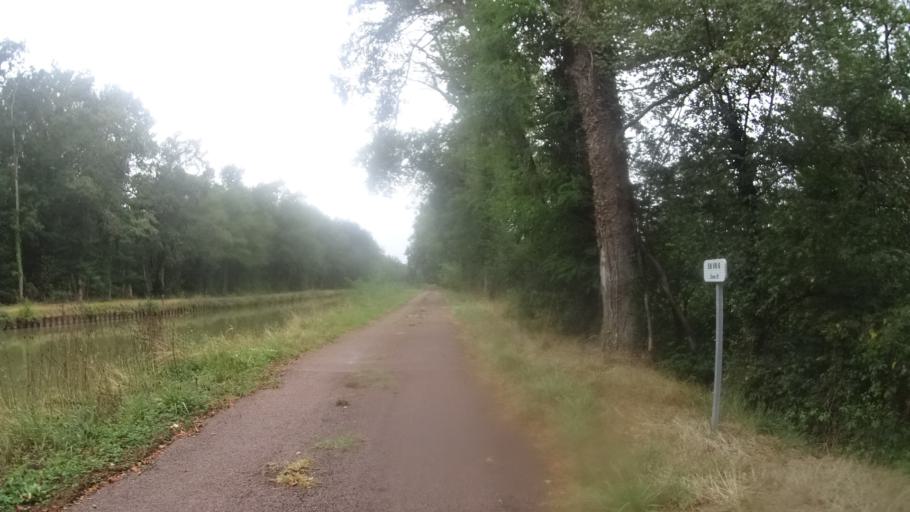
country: FR
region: Bourgogne
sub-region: Departement de la Nievre
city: Imphy
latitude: 46.8804
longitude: 3.2595
